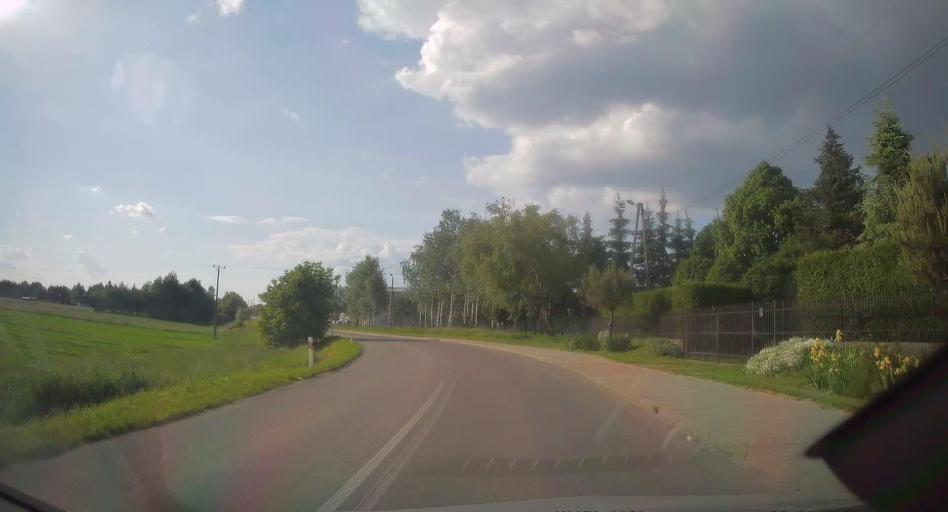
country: PL
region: Subcarpathian Voivodeship
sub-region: Powiat debicki
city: Zyrakow
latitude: 50.0688
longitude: 21.3999
